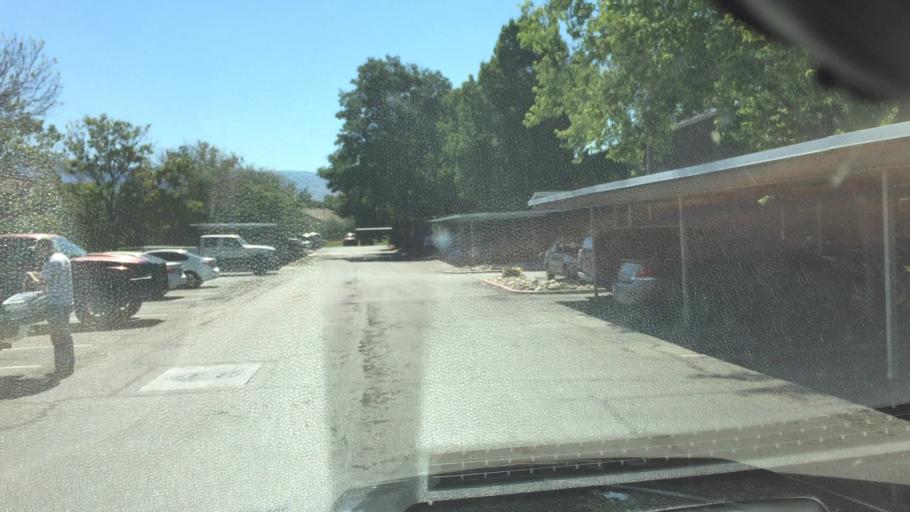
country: US
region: Nevada
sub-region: Washoe County
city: Sparks
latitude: 39.4820
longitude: -119.7446
